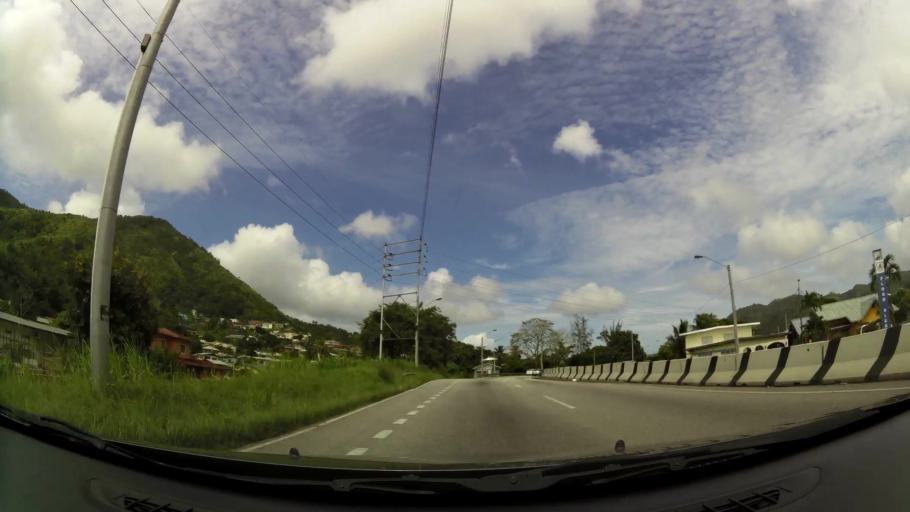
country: TT
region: Diego Martin
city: Petit Valley
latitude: 10.6979
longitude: -61.5542
